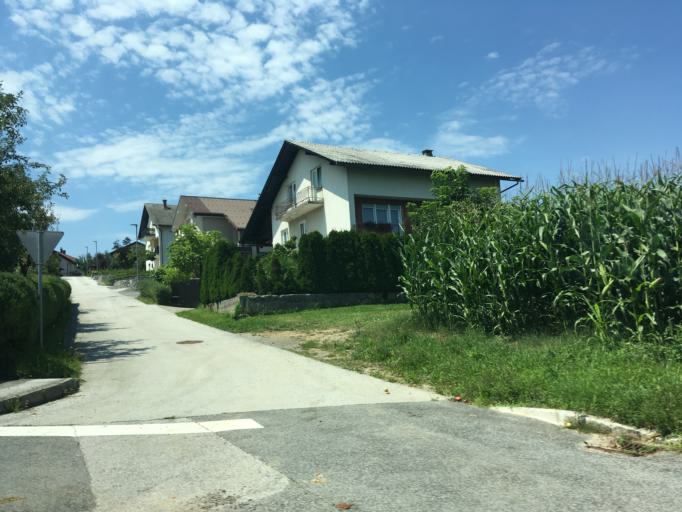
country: SI
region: Metlika
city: Metlika
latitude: 45.6475
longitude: 15.3251
